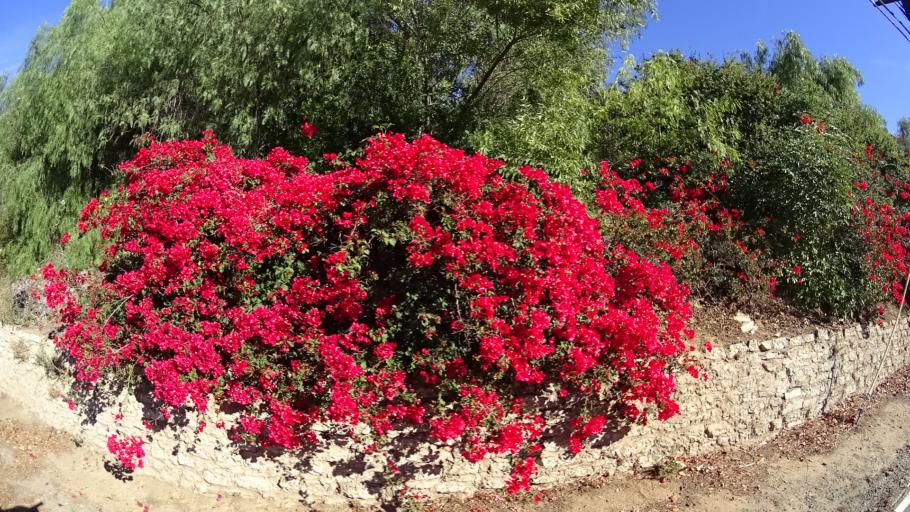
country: US
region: California
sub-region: Orange County
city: Villa Park
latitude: 33.8060
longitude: -117.8013
